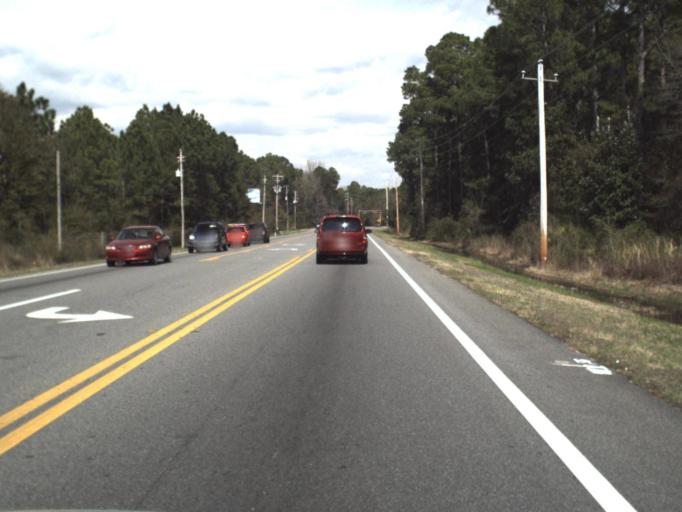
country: US
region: Florida
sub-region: Bay County
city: Lynn Haven
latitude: 30.2237
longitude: -85.6626
